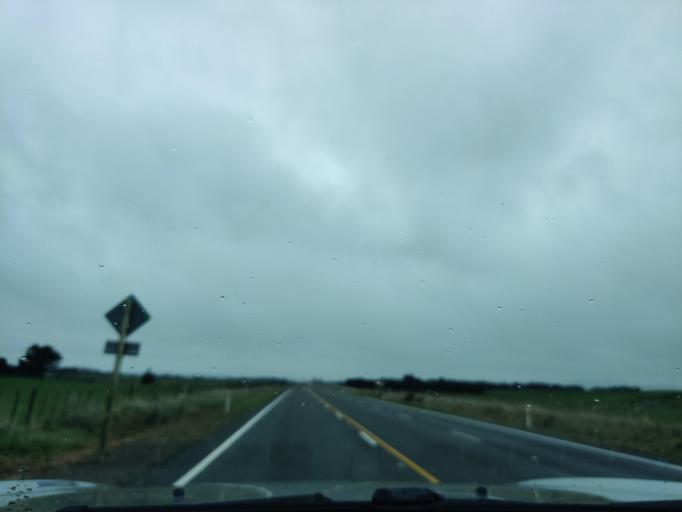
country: NZ
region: Hawke's Bay
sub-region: Hastings District
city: Hastings
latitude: -40.0205
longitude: 176.2985
